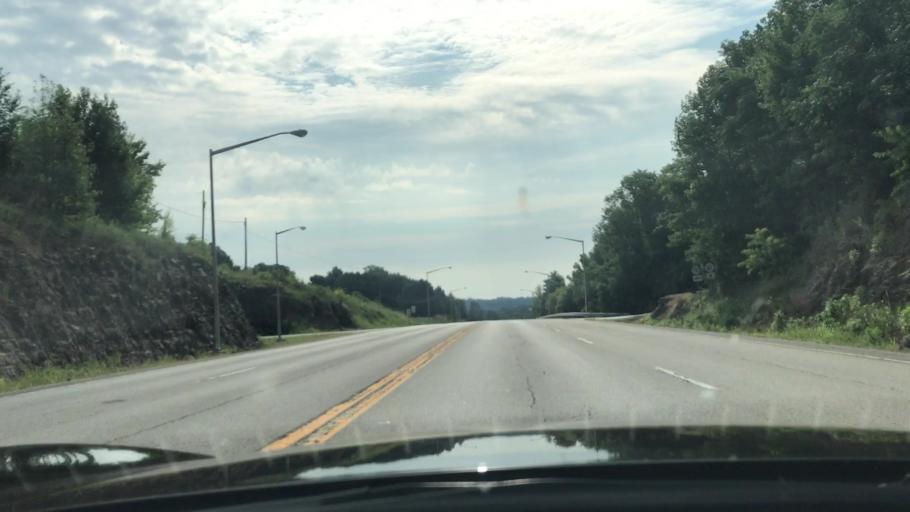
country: US
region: Kentucky
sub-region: Green County
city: Greensburg
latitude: 37.2730
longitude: -85.5042
